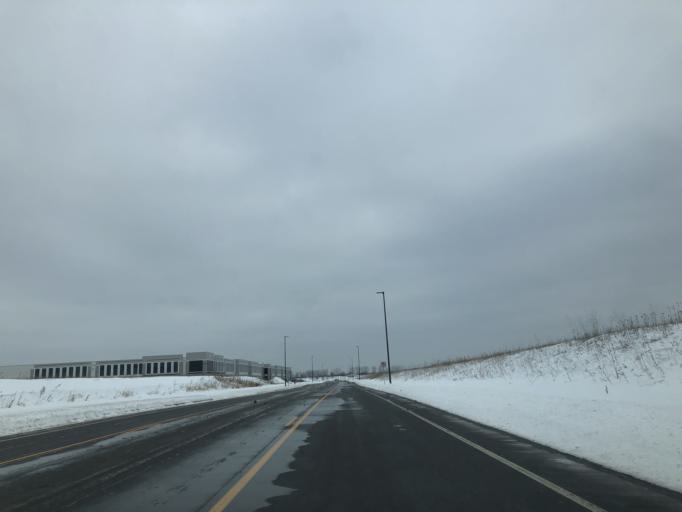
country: US
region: Minnesota
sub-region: Hennepin County
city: Osseo
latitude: 45.0920
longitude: -93.4192
